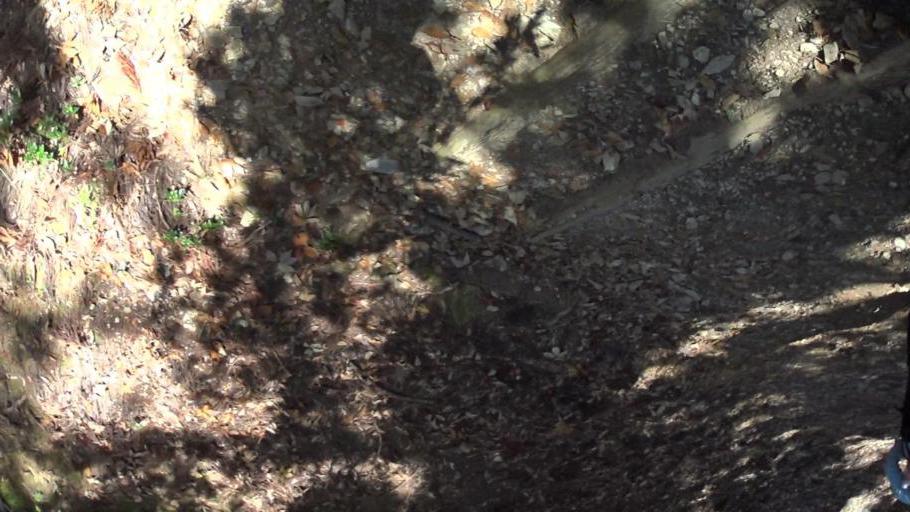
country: JP
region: Kyoto
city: Kameoka
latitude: 35.0467
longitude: 135.6417
